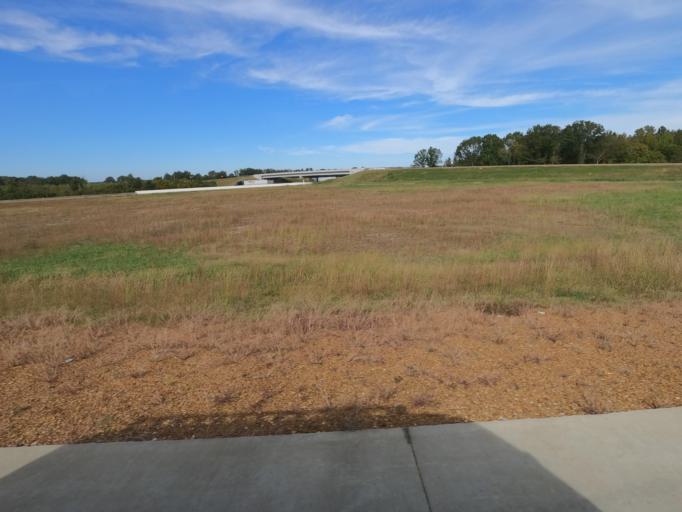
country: US
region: Tennessee
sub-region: Fayette County
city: Hickory Withe
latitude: 35.2898
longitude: -89.6098
